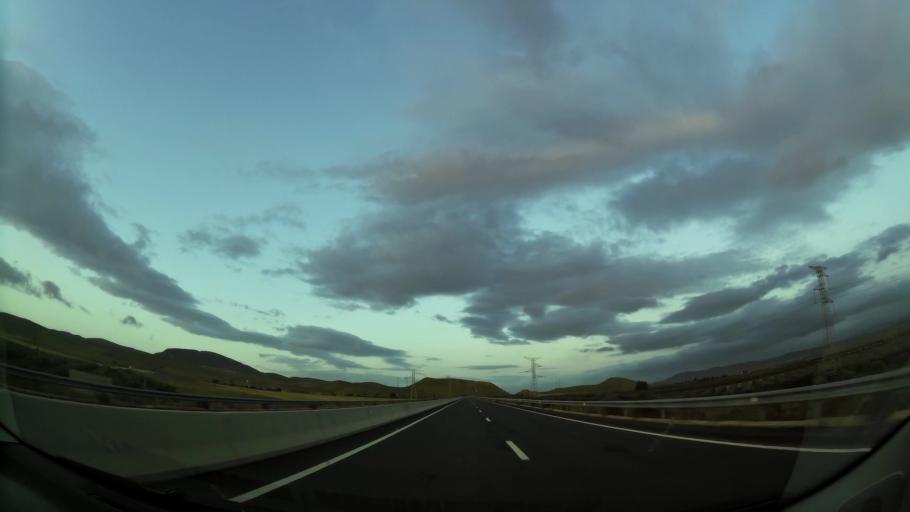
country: MA
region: Oriental
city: El Aioun
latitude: 34.5946
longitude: -2.6831
